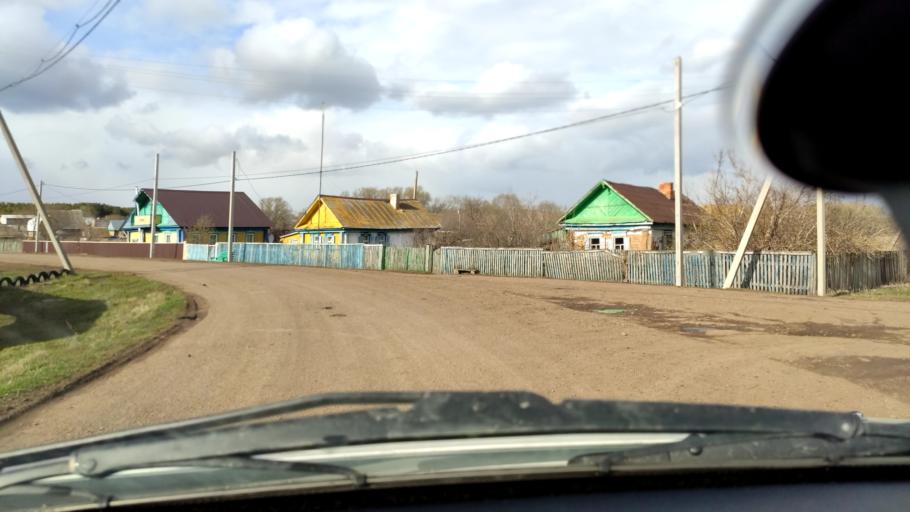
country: RU
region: Bashkortostan
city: Buzdyak
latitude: 54.7690
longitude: 54.6252
